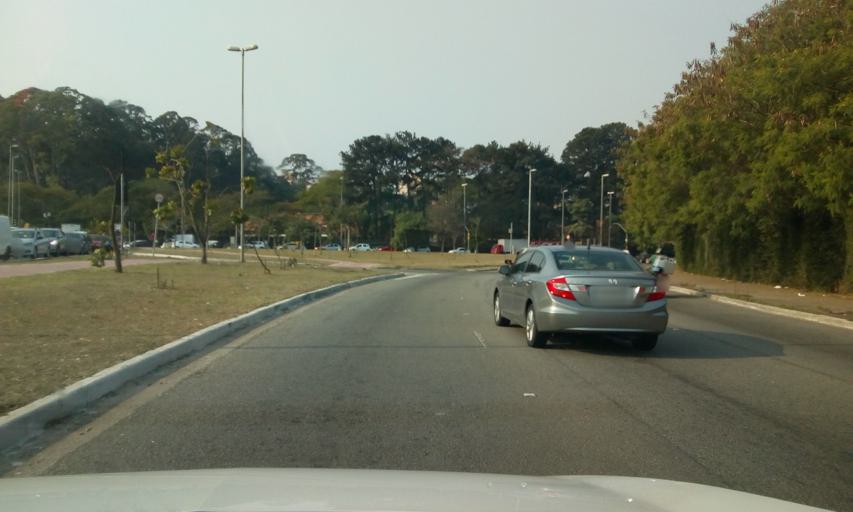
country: BR
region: Sao Paulo
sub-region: Diadema
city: Diadema
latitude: -23.6952
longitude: -46.6835
